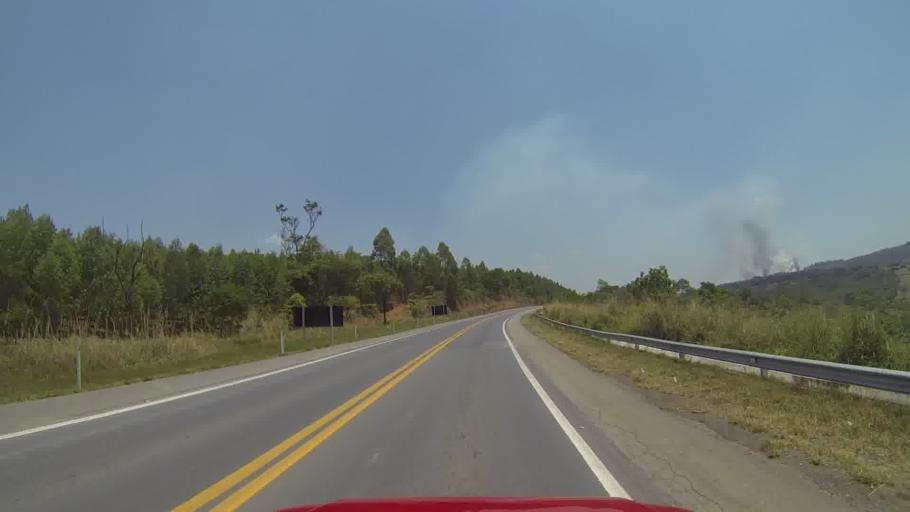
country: BR
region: Minas Gerais
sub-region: Itapecerica
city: Itapecerica
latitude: -20.3429
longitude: -45.2532
